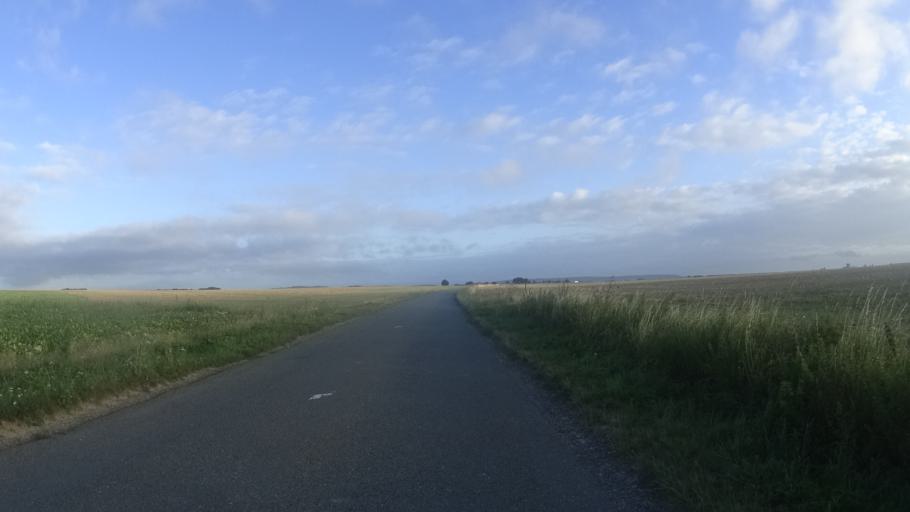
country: FR
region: Picardie
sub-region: Departement de l'Oise
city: Chamant
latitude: 49.1931
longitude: 2.6697
